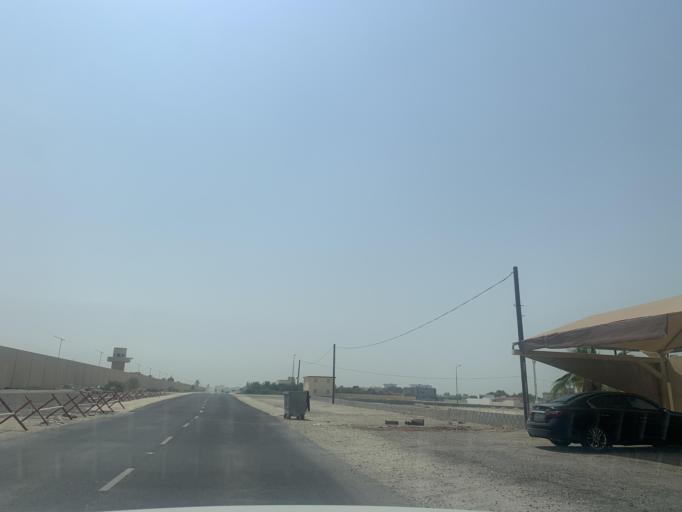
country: BH
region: Central Governorate
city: Madinat Hamad
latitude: 26.1517
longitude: 50.4736
